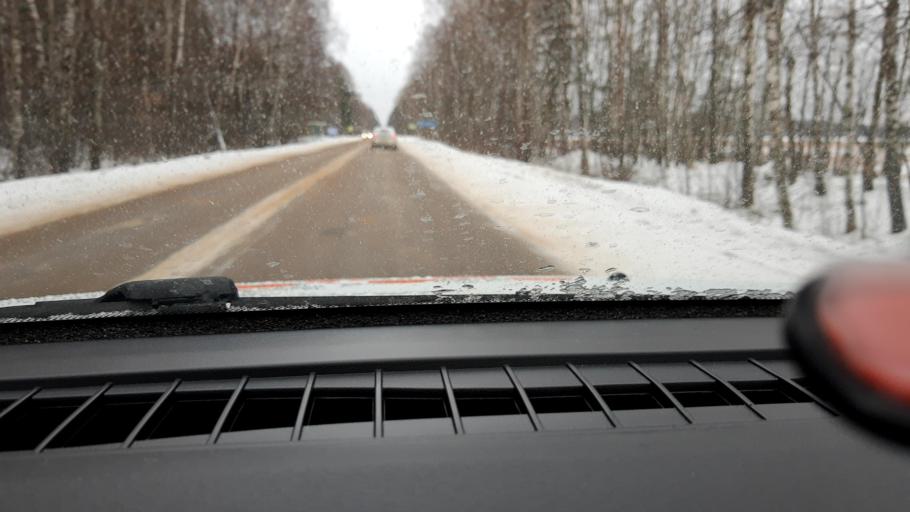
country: RU
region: Nizjnij Novgorod
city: Kstovo
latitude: 56.2959
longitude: 44.2748
